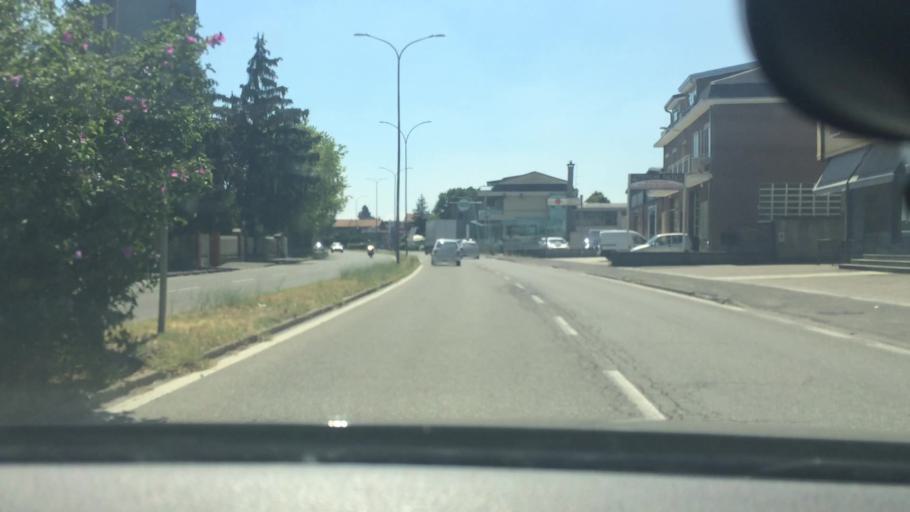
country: IT
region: Emilia-Romagna
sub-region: Provincia di Piacenza
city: Piacenza
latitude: 45.0494
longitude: 9.6632
